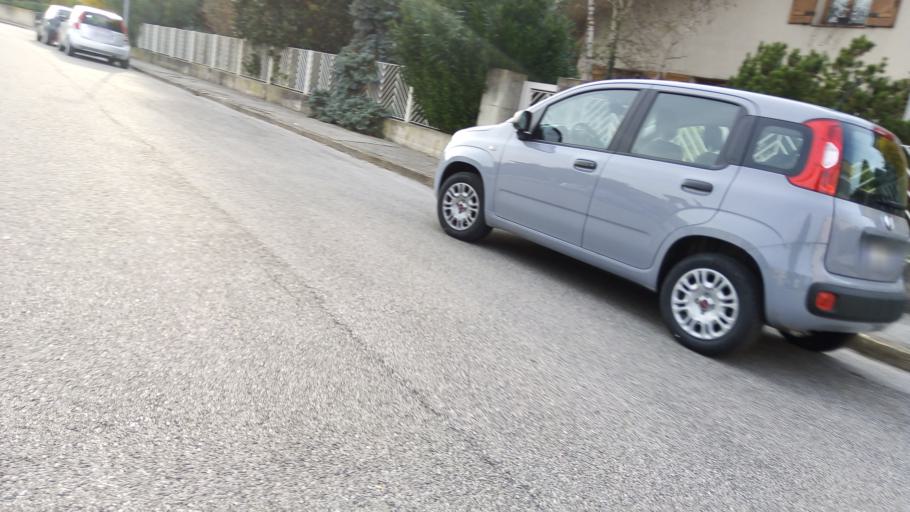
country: IT
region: Veneto
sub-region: Provincia di Padova
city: Abano Terme
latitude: 45.3584
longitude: 11.7804
